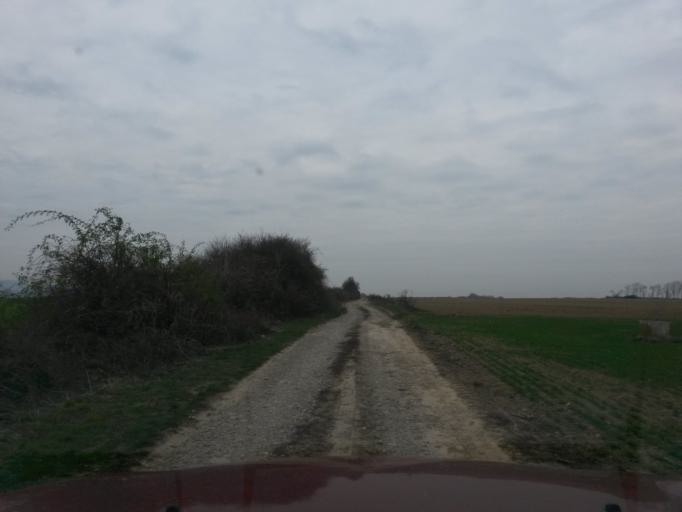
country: SK
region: Kosicky
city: Secovce
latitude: 48.6586
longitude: 21.6692
